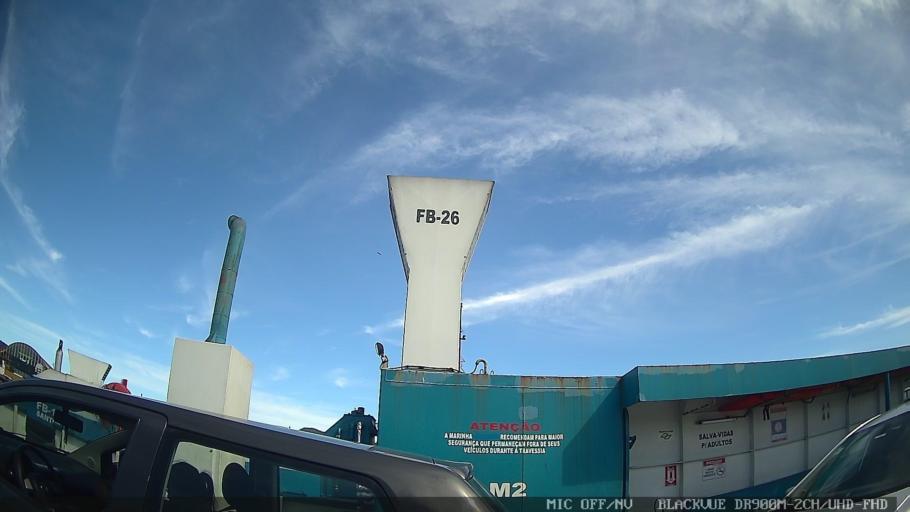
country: BR
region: Sao Paulo
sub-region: Guaruja
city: Guaruja
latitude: -23.9873
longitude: -46.2903
